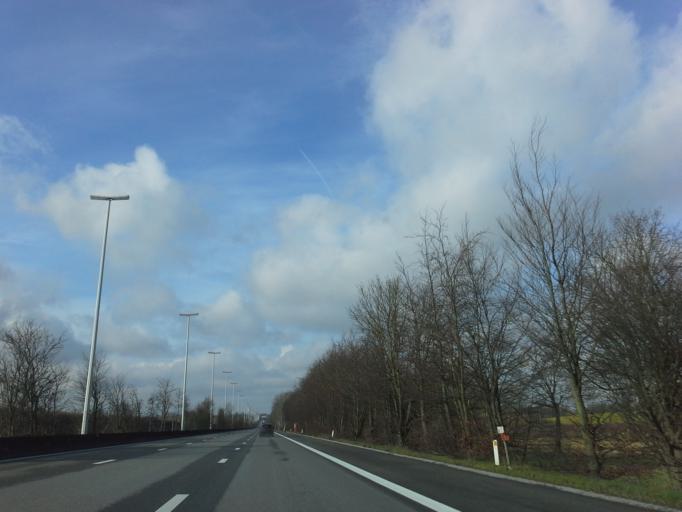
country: BE
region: Flanders
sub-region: Provincie Vlaams-Brabant
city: Bierbeek
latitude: 50.8355
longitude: 4.7753
